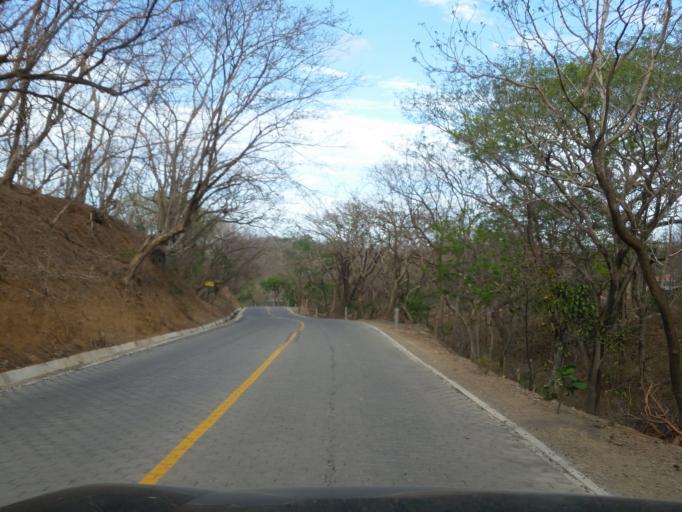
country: NI
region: Rivas
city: Tola
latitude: 11.3912
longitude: -85.9838
